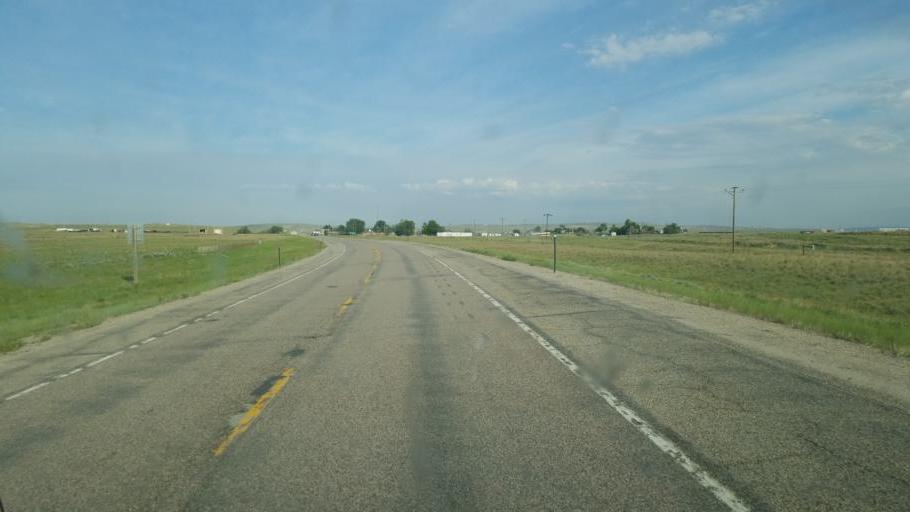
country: US
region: Wyoming
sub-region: Natrona County
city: Mills
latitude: 43.0318
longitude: -106.9780
